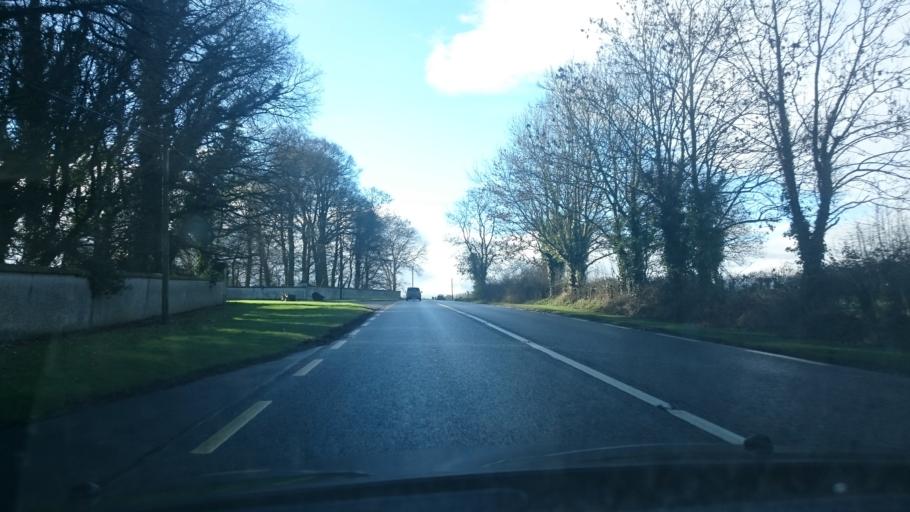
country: IE
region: Leinster
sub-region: Kilkenny
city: Callan
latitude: 52.5837
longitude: -7.3142
